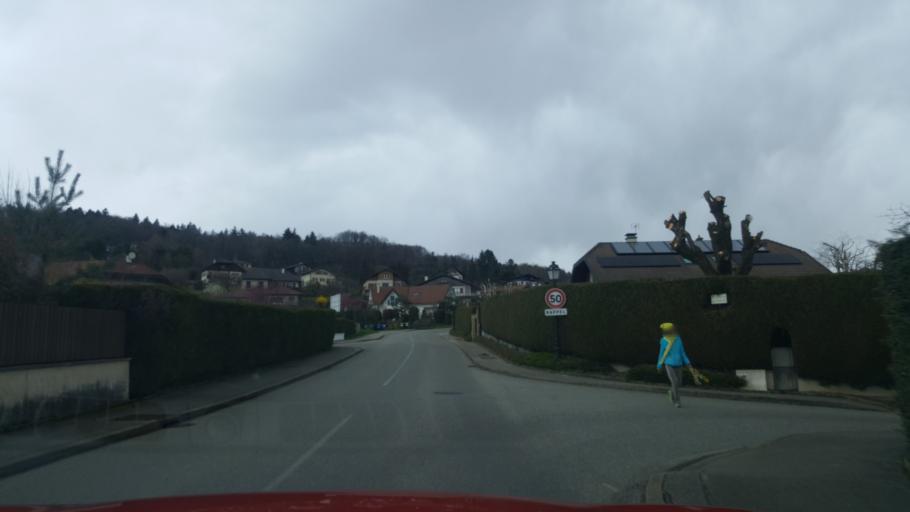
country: FR
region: Rhone-Alpes
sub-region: Departement de la Haute-Savoie
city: Epagny
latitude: 45.9447
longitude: 6.0865
